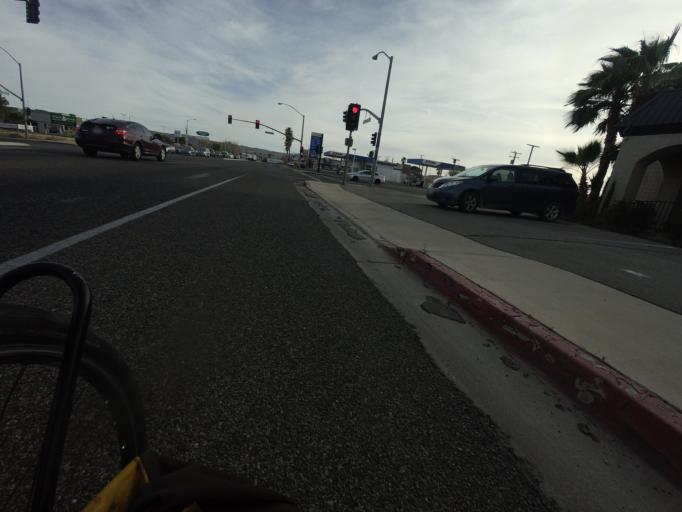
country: US
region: California
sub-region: Kern County
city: Ridgecrest
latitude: 35.6251
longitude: -117.6701
